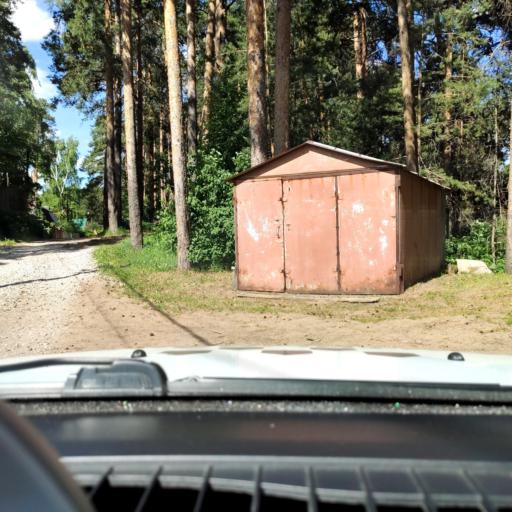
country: RU
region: Perm
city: Perm
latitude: 58.0625
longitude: 56.3088
